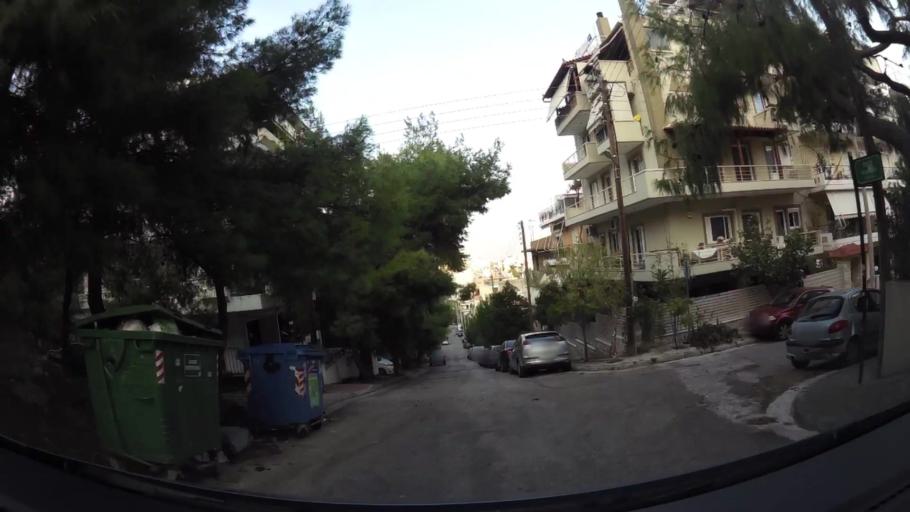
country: GR
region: Attica
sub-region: Nomarchia Athinas
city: Petroupolis
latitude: 38.0395
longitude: 23.6675
